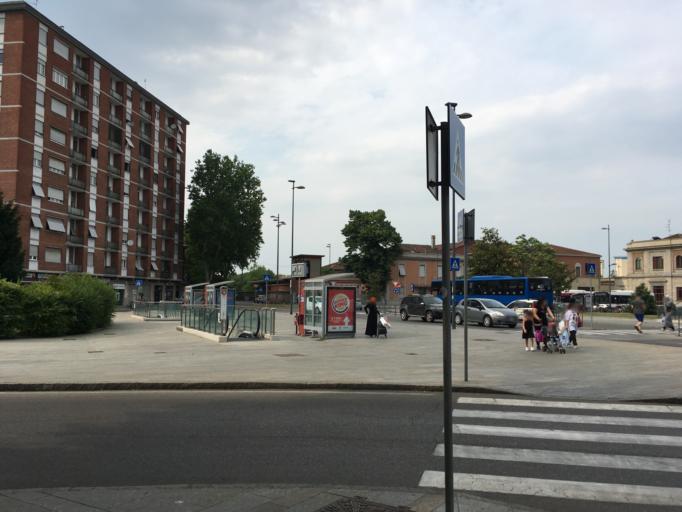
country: IT
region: Emilia-Romagna
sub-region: Provincia di Piacenza
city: Piacenza
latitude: 45.0513
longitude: 9.7050
